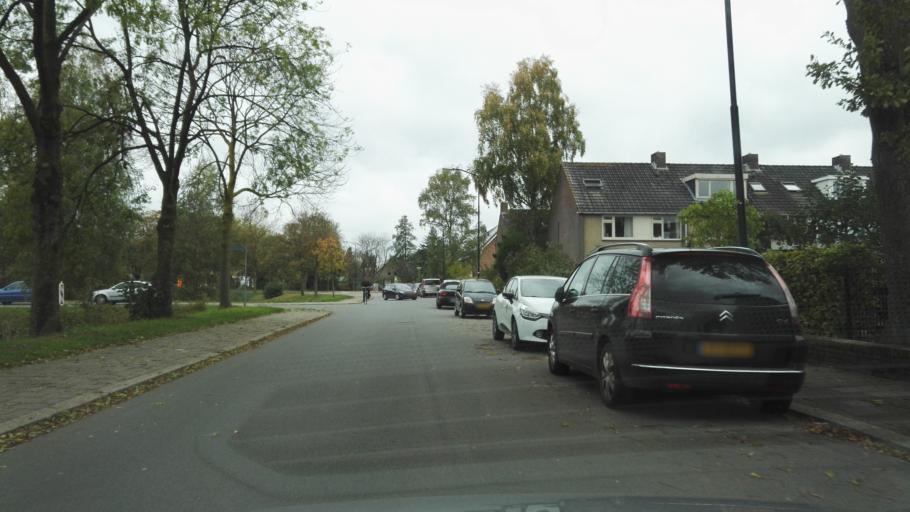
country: NL
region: Gelderland
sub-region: Gemeente Apeldoorn
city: Apeldoorn
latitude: 52.2262
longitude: 6.0004
